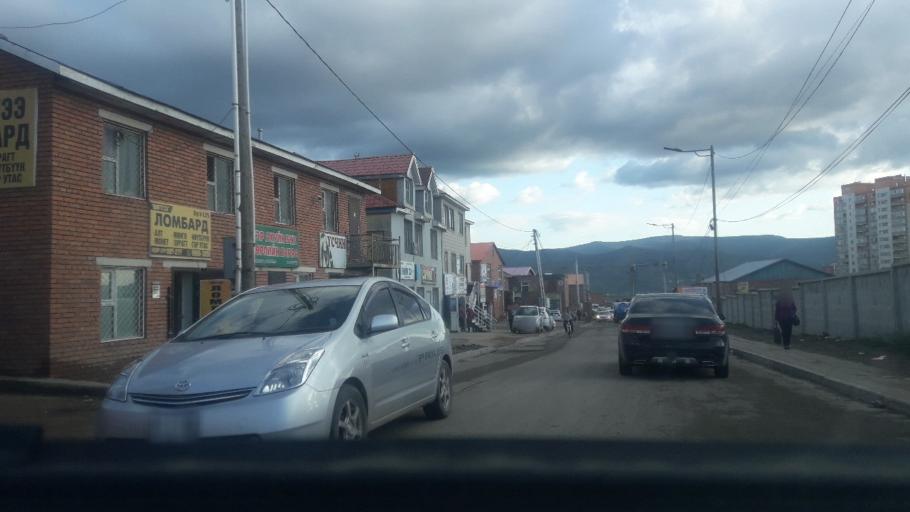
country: MN
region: Ulaanbaatar
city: Ulaanbaatar
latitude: 47.9236
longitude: 106.9962
